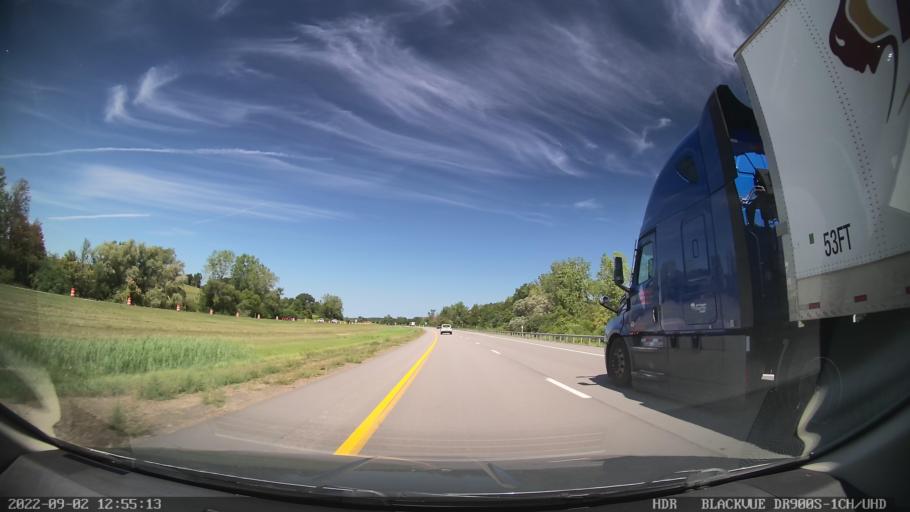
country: US
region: New York
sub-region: Livingston County
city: Avon
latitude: 42.9369
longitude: -77.6908
